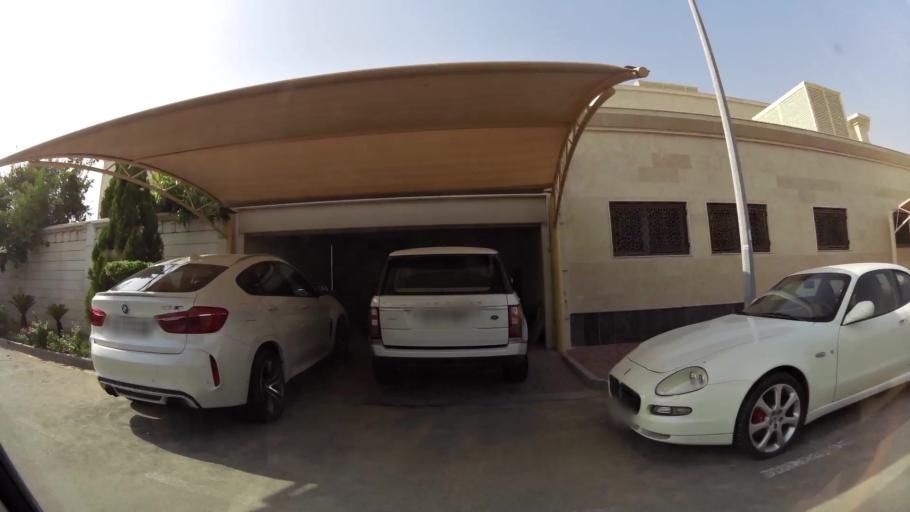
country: AE
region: Ash Shariqah
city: Sharjah
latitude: 25.2573
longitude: 55.4497
